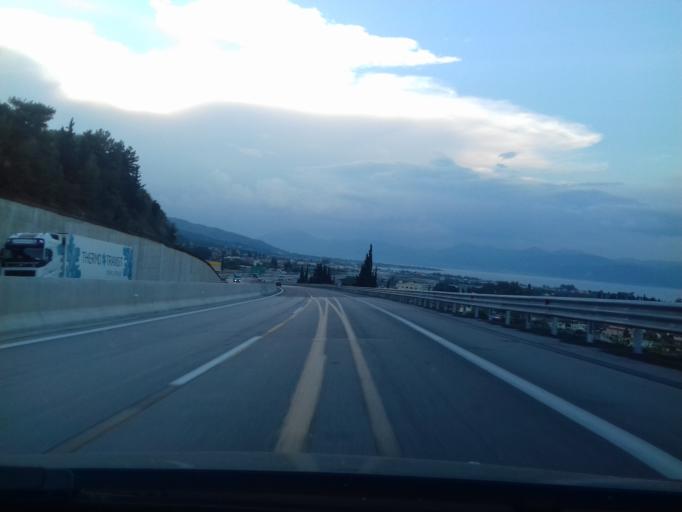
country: GR
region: West Greece
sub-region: Nomos Achaias
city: Aigio
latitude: 38.2547
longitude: 22.0679
